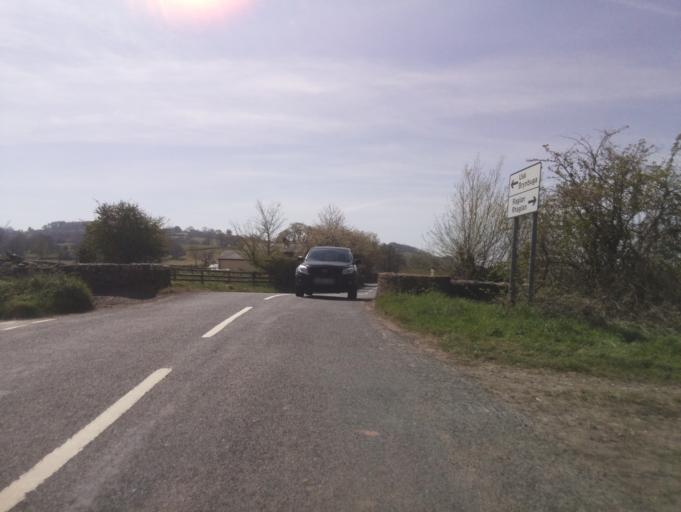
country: GB
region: Wales
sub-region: Monmouthshire
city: Llangwm
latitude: 51.7190
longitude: -2.8420
